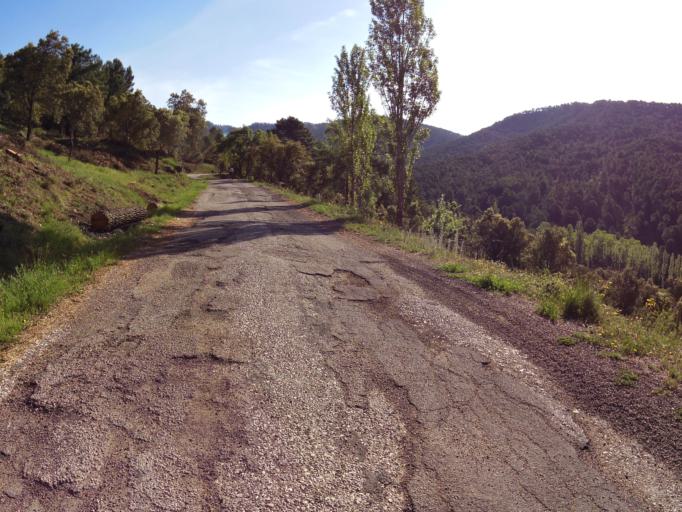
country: ES
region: Castille-La Mancha
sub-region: Provincia de Albacete
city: Riopar
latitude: 38.5180
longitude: -2.4561
